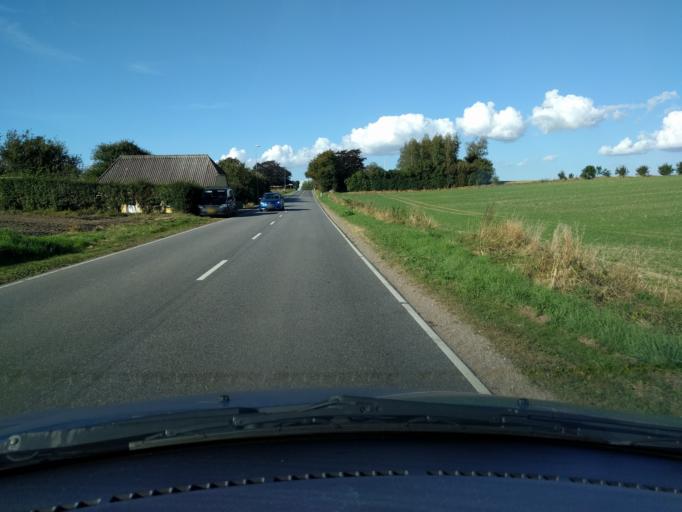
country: DK
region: South Denmark
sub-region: Assens Kommune
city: Assens
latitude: 55.2527
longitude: 9.9834
